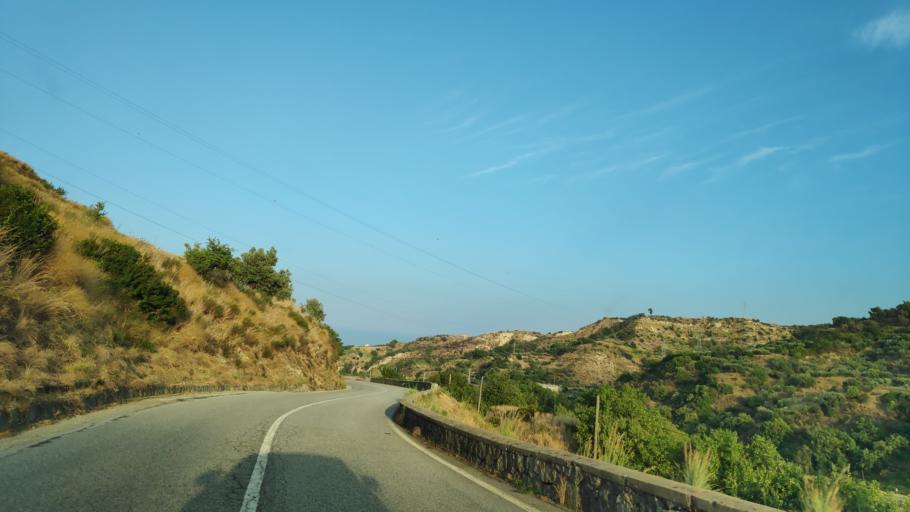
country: IT
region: Calabria
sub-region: Provincia di Catanzaro
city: Satriano
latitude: 38.6748
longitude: 16.5012
